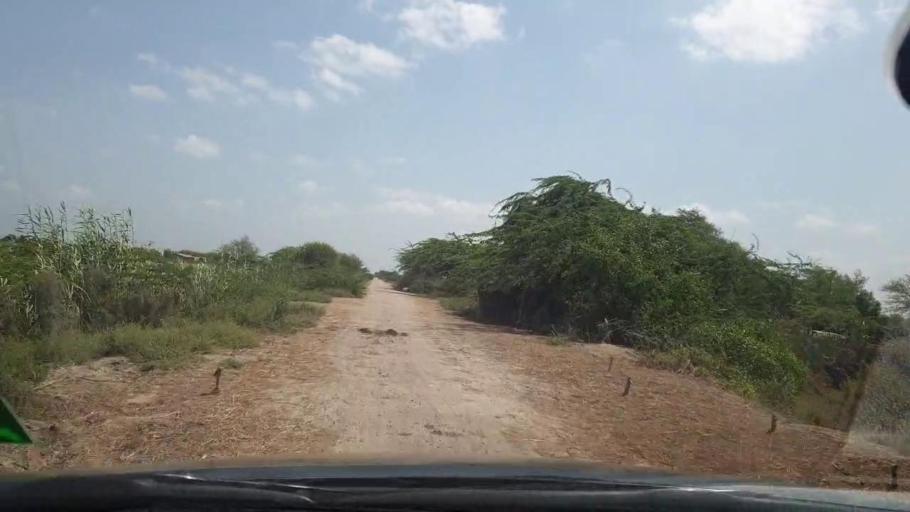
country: PK
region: Sindh
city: Tando Bago
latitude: 24.8619
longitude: 69.0972
